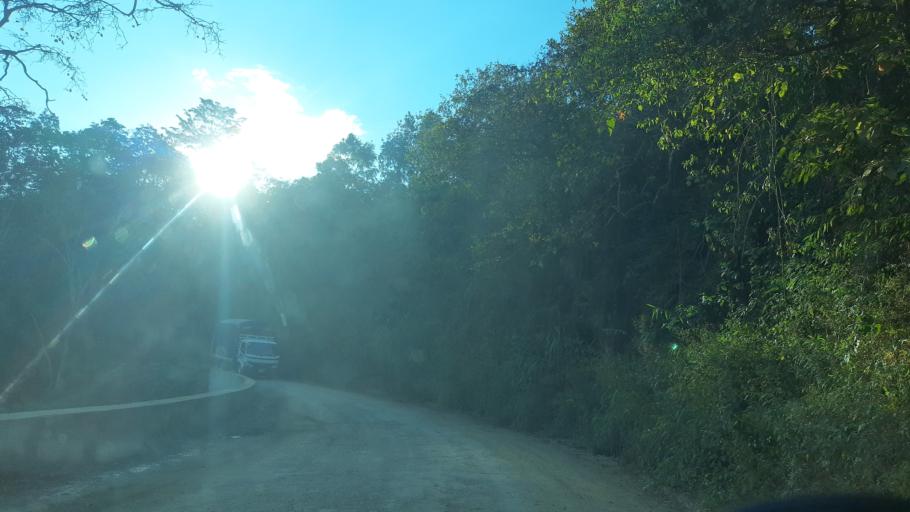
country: CO
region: Boyaca
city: Garagoa
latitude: 5.0824
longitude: -73.3888
